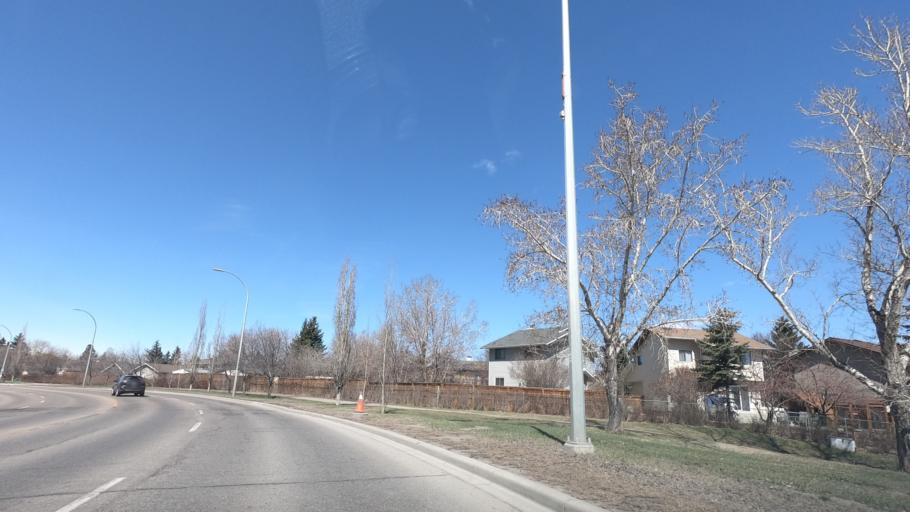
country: CA
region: Alberta
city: Airdrie
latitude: 51.2722
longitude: -114.0084
